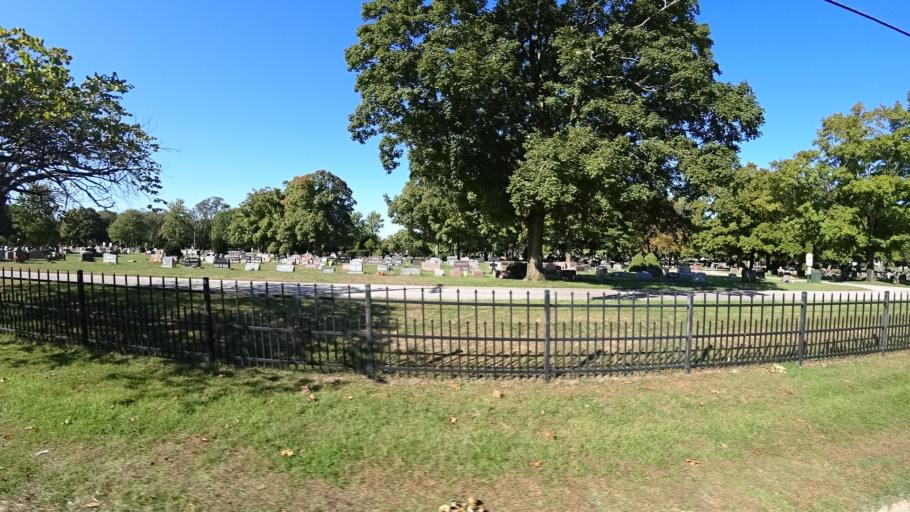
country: US
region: Indiana
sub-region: LaPorte County
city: Michigan City
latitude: 41.7032
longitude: -86.8795
